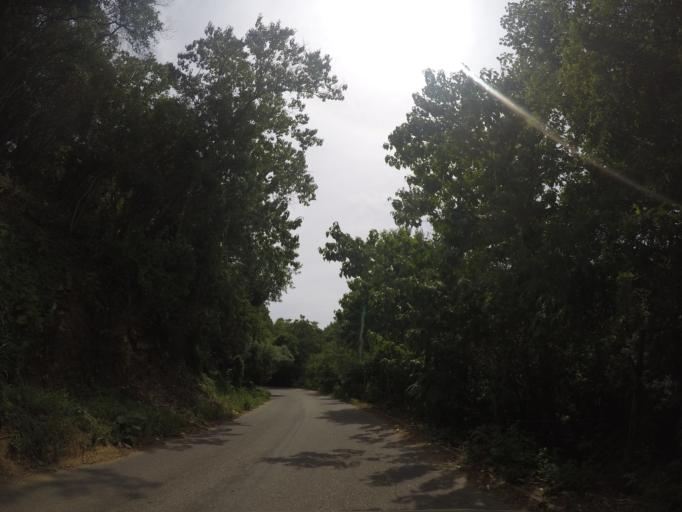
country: MX
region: Oaxaca
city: Santa Maria Tonameca
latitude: 15.6677
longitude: -96.5340
